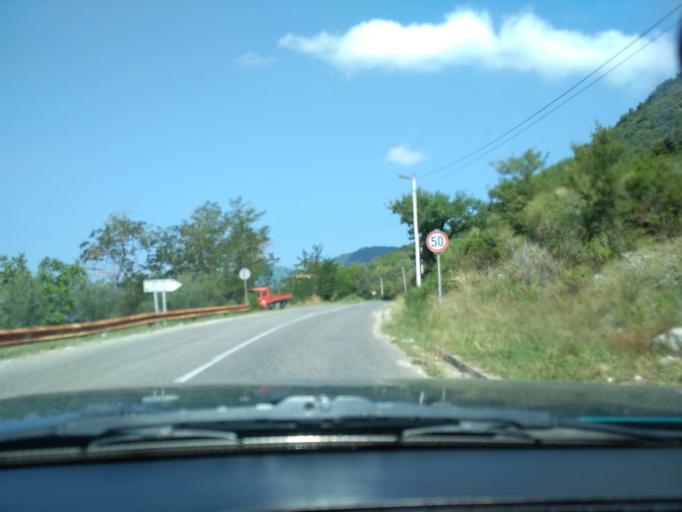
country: ME
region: Kotor
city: Kotor
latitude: 42.3902
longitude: 18.7573
